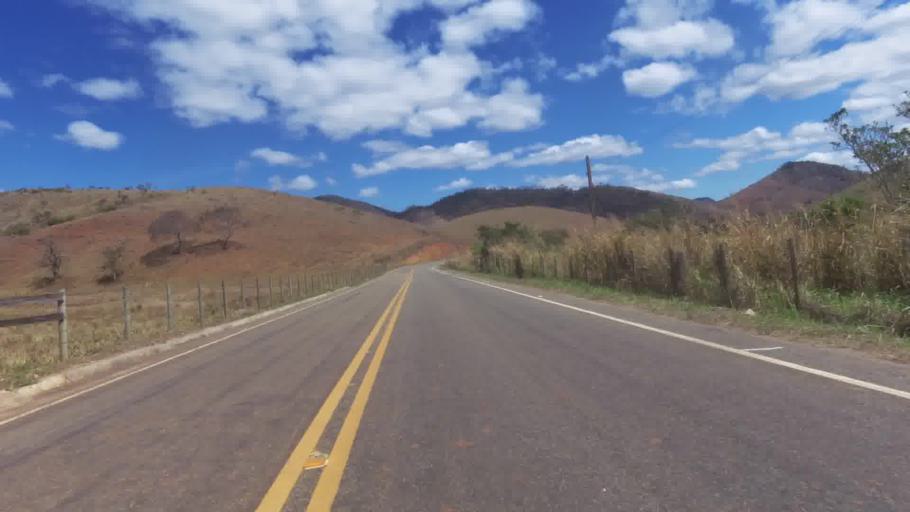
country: BR
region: Espirito Santo
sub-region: Cachoeiro De Itapemirim
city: Cachoeiro de Itapemirim
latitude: -20.9160
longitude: -41.2305
